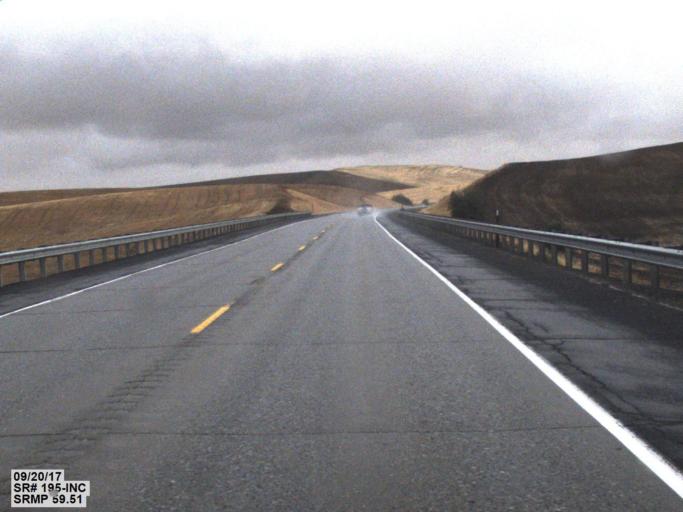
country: US
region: Washington
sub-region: Whitman County
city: Colfax
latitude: 47.1677
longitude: -117.3795
